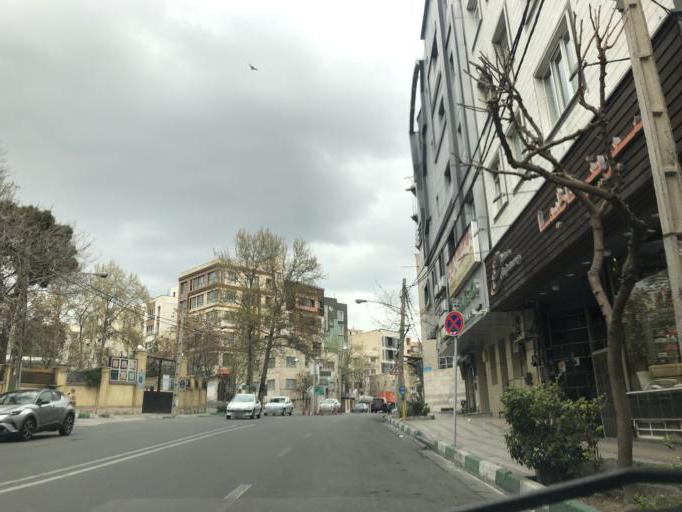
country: IR
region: Tehran
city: Tajrish
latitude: 35.7786
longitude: 51.4441
